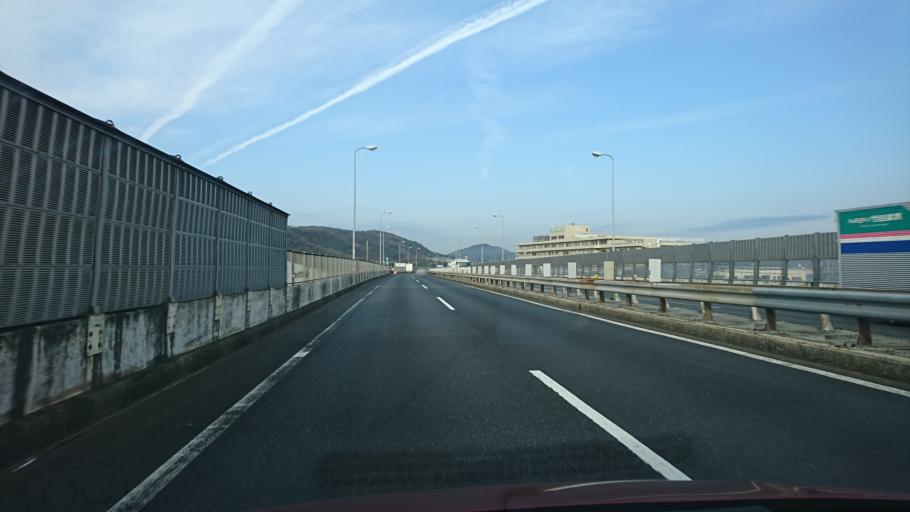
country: JP
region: Hyogo
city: Shirahamacho-usazakiminami
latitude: 34.7877
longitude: 134.7742
